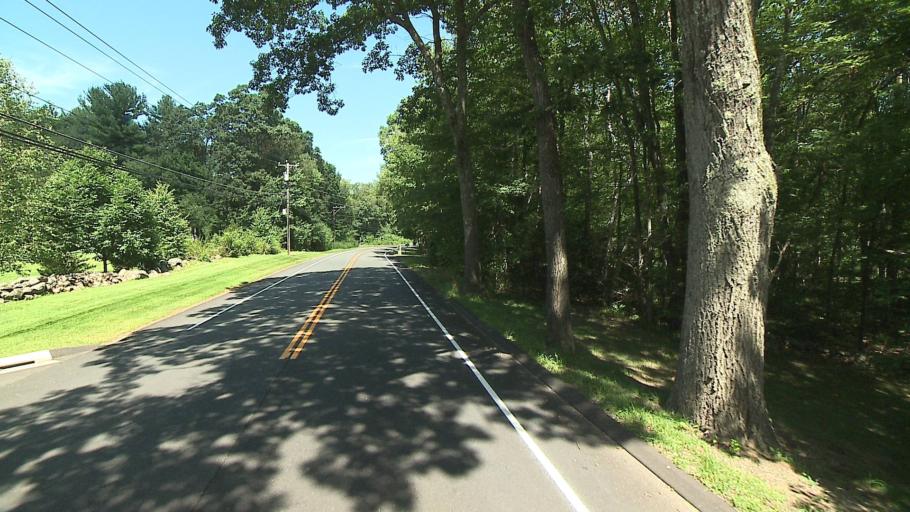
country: US
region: Connecticut
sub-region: Hartford County
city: North Granby
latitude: 41.9609
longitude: -72.9173
